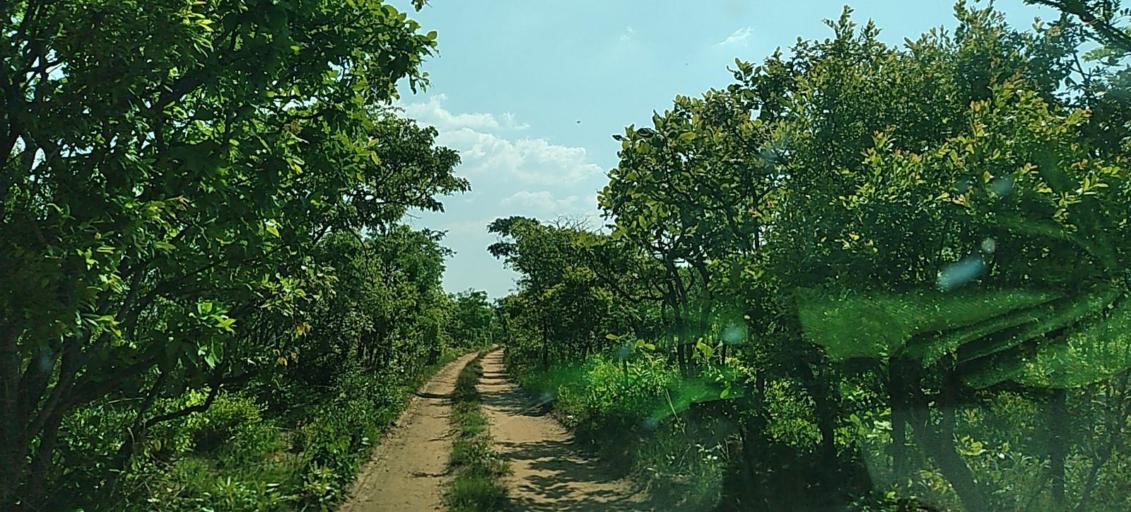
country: CD
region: Katanga
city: Kolwezi
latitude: -11.2686
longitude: 24.9951
